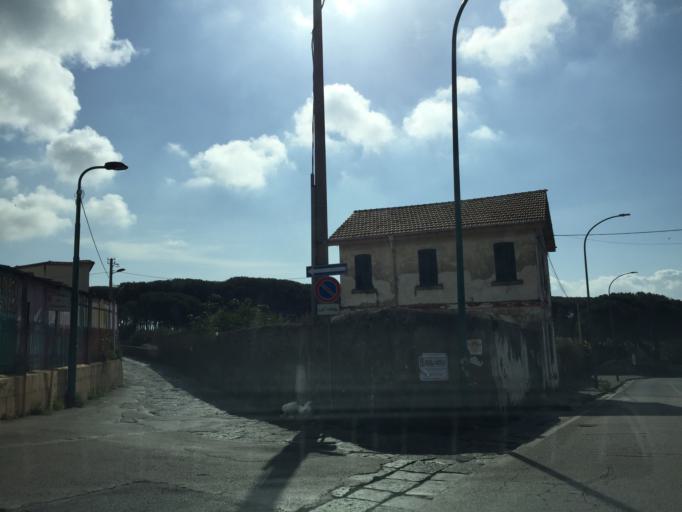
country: IT
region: Campania
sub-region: Provincia di Napoli
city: Torre del Greco
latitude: 40.7803
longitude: 14.4084
